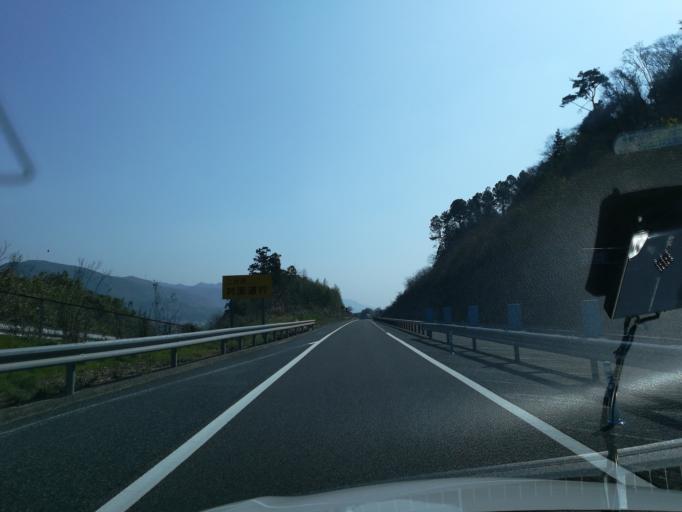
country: JP
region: Tokushima
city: Ikedacho
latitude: 34.0305
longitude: 133.8485
